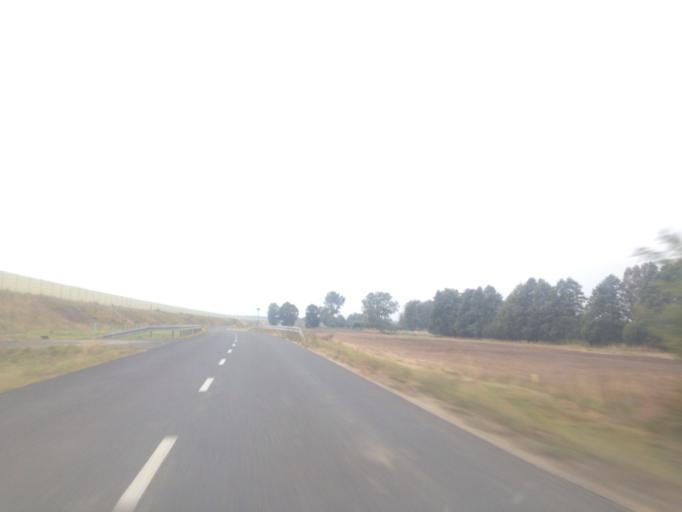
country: PL
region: Greater Poland Voivodeship
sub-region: Powiat gnieznienski
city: Lubowo
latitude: 52.4682
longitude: 17.4030
